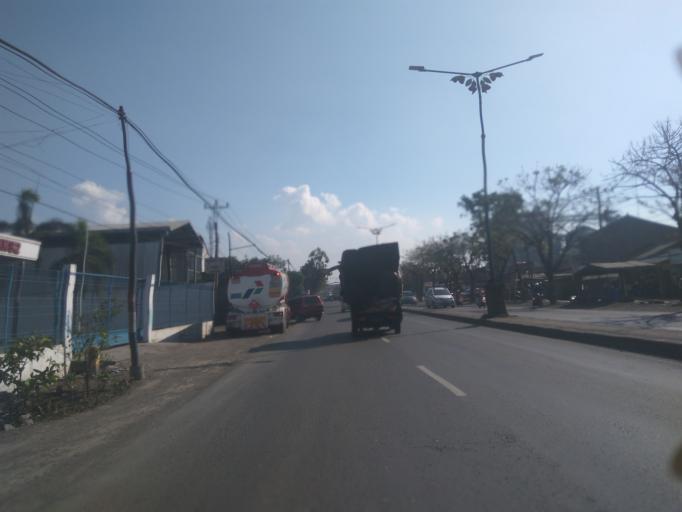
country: ID
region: Central Java
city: Mranggen
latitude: -6.9467
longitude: 110.4937
